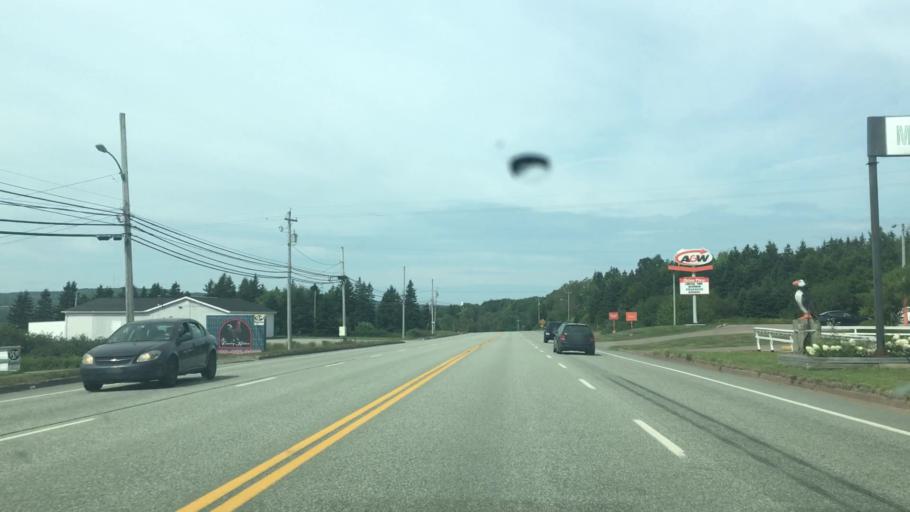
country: CA
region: Nova Scotia
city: Port Hawkesbury
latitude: 45.6415
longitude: -61.3898
